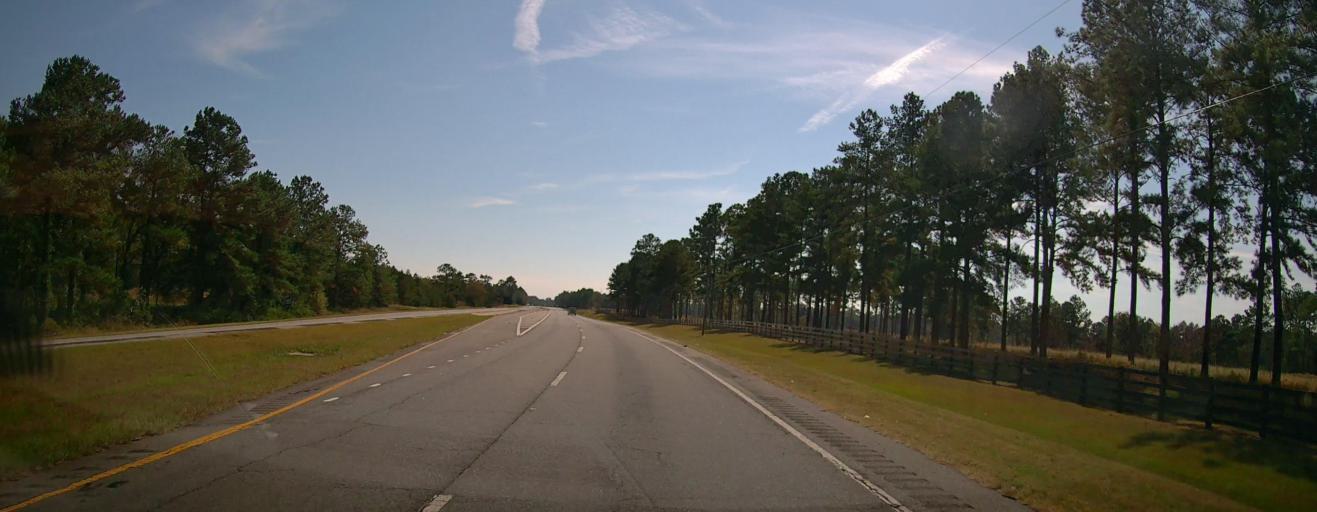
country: US
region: Georgia
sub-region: Lee County
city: Leesburg
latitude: 31.7497
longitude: -83.9880
